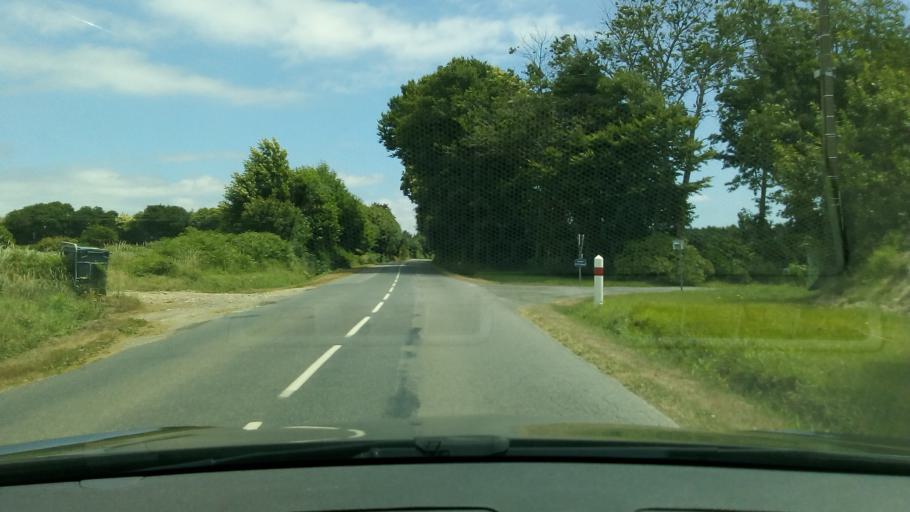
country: FR
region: Brittany
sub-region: Departement du Finistere
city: Tregunc
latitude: 47.8788
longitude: -3.8697
